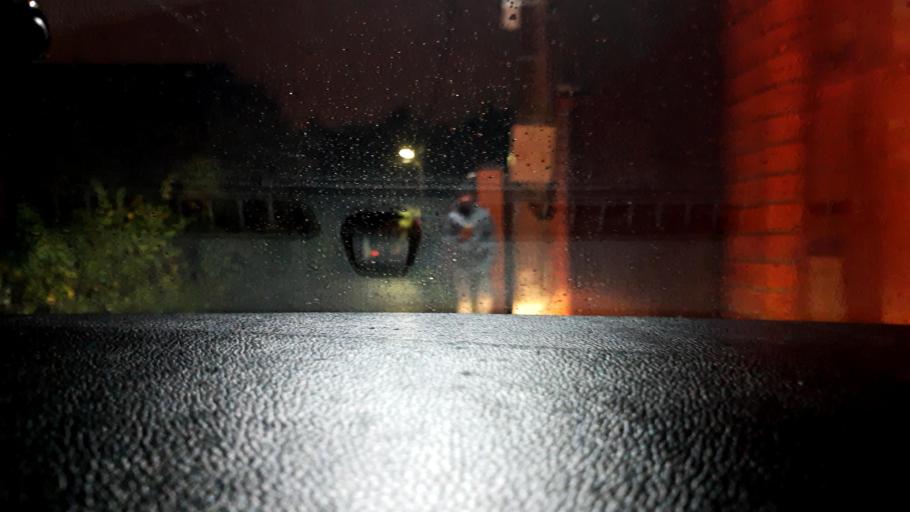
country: RU
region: Moskovskaya
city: Mosrentgen
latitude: 55.6261
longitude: 37.4677
